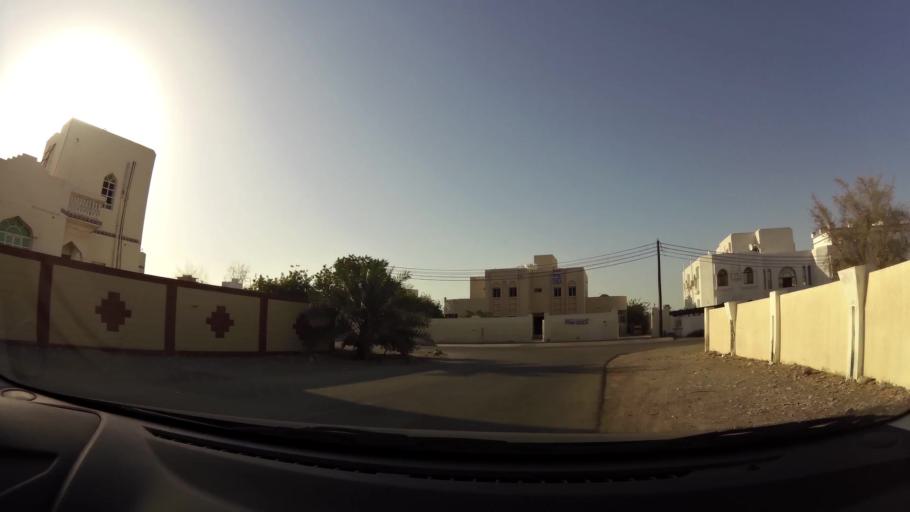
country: OM
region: Muhafazat Masqat
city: As Sib al Jadidah
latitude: 23.6394
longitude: 58.1997
